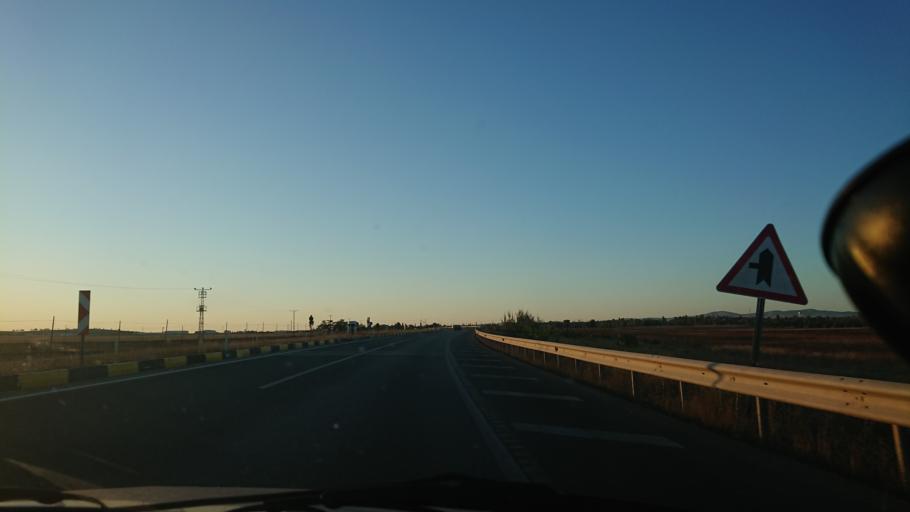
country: TR
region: Eskisehir
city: Mahmudiye
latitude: 39.5535
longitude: 30.9240
